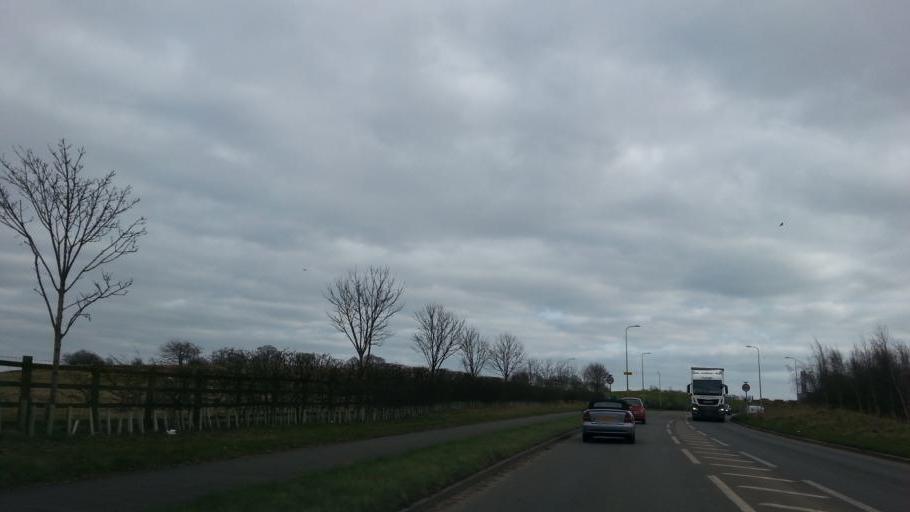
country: GB
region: England
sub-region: Staffordshire
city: Rugeley
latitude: 52.7763
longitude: -1.9530
